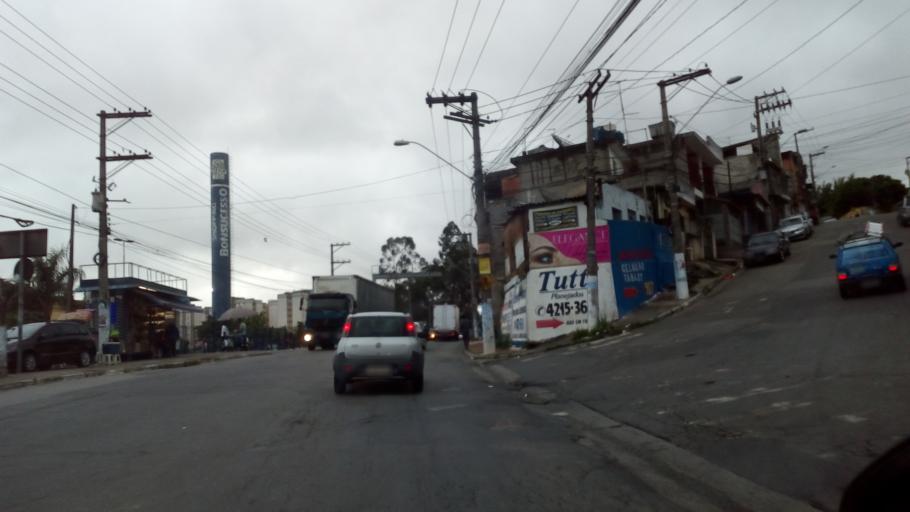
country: BR
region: Sao Paulo
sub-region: Itaquaquecetuba
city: Itaquaquecetuba
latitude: -23.4332
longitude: -46.4054
